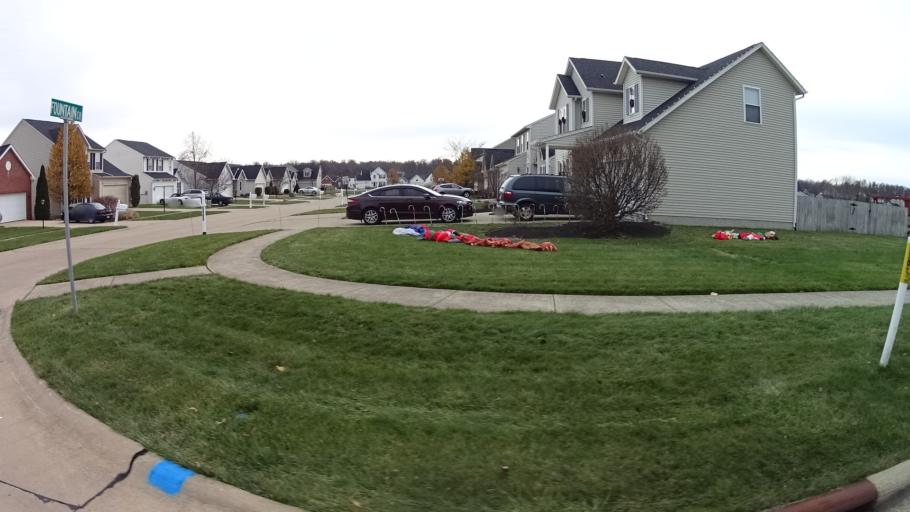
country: US
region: Ohio
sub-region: Lorain County
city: Sheffield
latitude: 41.4118
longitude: -82.0589
